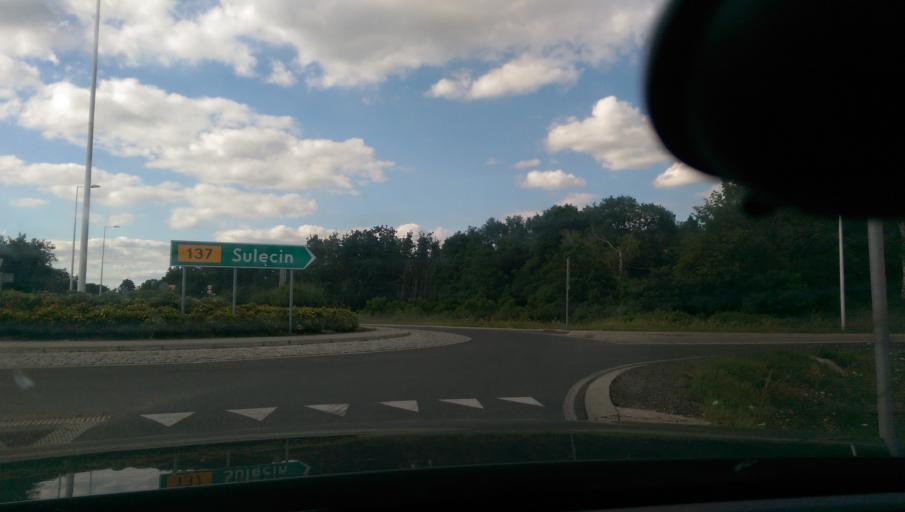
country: PL
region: Lubusz
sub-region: Powiat slubicki
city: Osno Lubuskie
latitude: 52.4561
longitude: 14.8940
